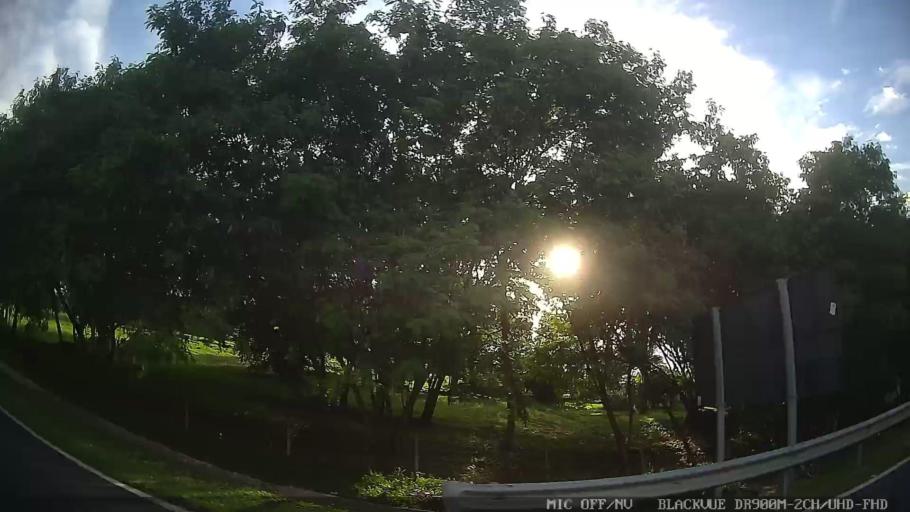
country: BR
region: Sao Paulo
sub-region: Tiete
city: Tiete
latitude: -23.1154
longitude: -47.7189
